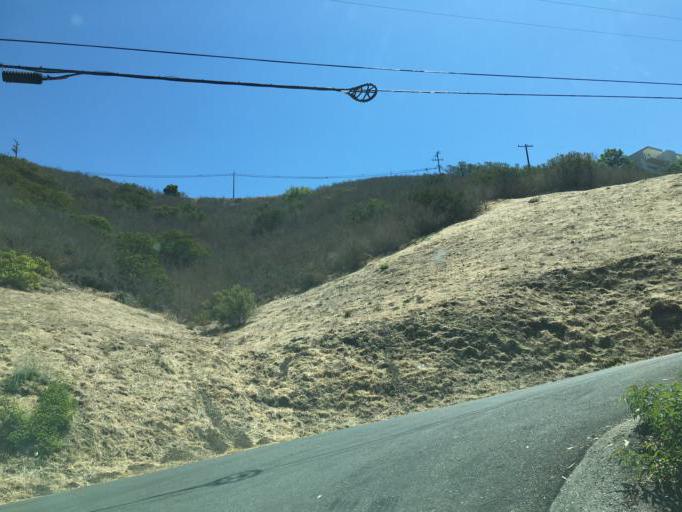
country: US
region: California
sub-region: Los Angeles County
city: Malibu Beach
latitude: 34.0489
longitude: -118.7412
